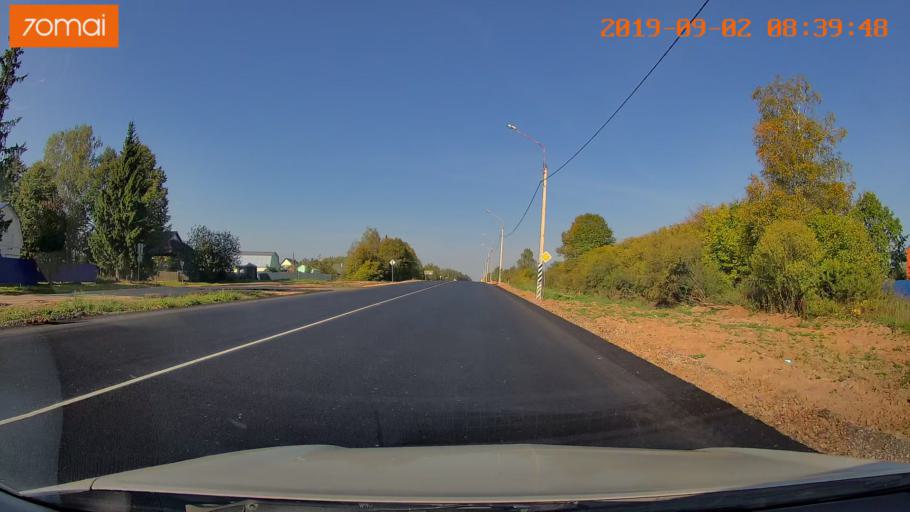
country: RU
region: Kaluga
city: Kudinovo
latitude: 54.9747
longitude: 36.1515
